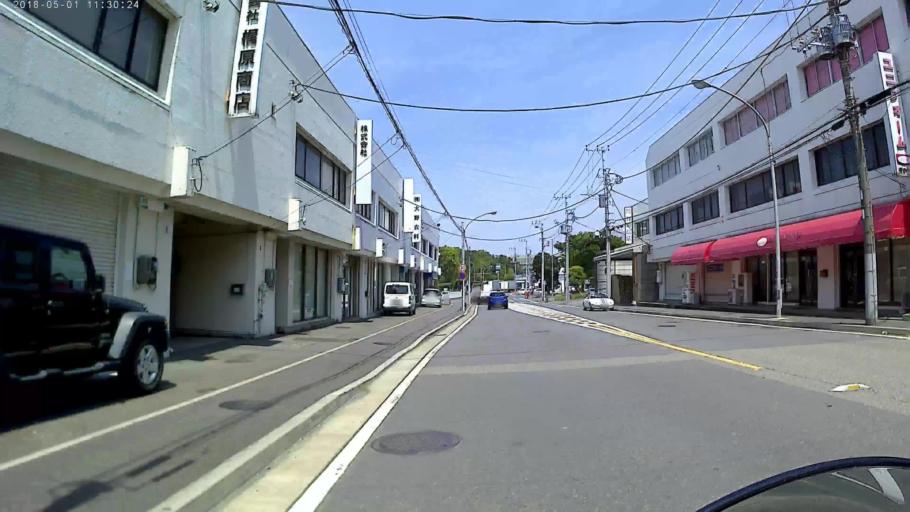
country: JP
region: Kanagawa
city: Minami-rinkan
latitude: 35.5010
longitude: 139.4863
